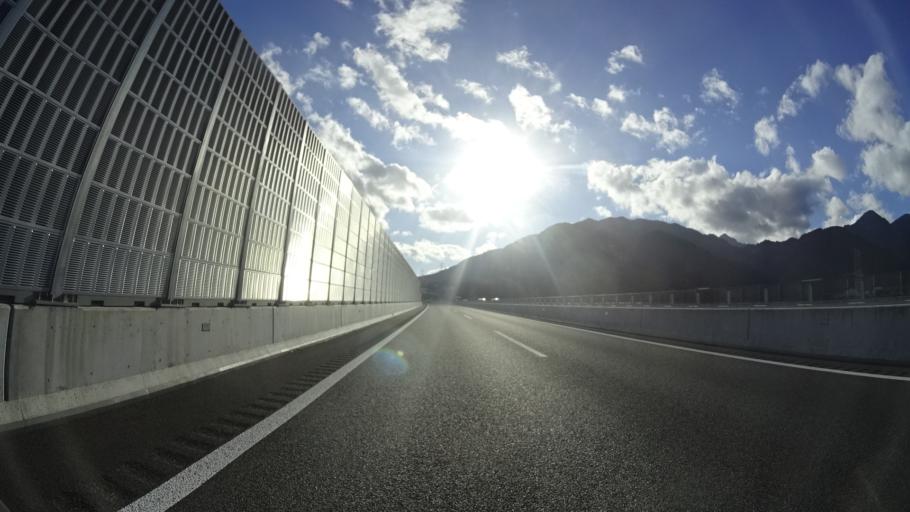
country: JP
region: Mie
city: Komono
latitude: 35.0145
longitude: 136.4828
